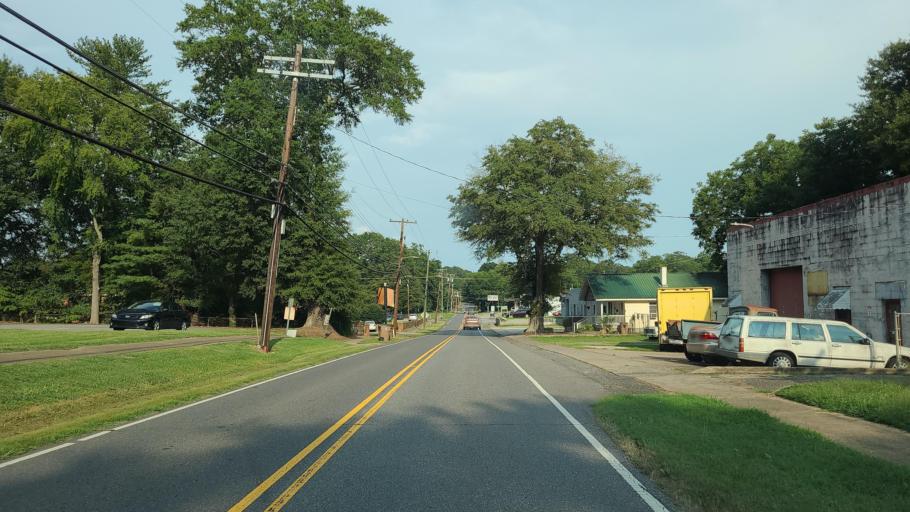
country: US
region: North Carolina
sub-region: Cleveland County
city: Shelby
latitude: 35.2926
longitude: -81.5558
